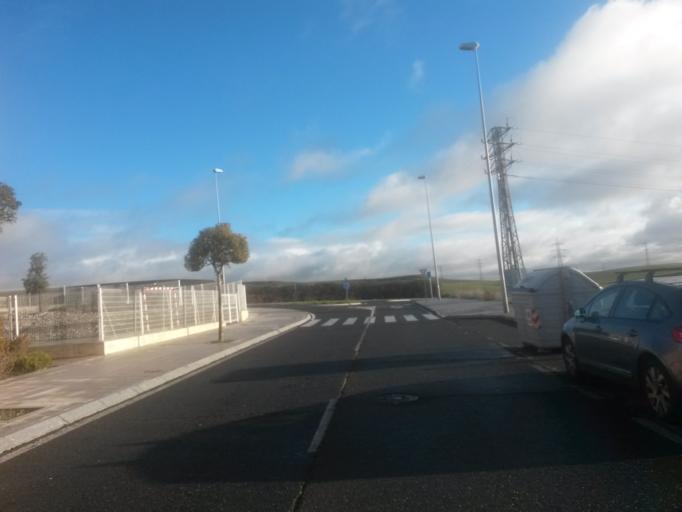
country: ES
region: Castille and Leon
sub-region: Provincia de Salamanca
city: Salamanca
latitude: 40.9784
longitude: -5.6442
